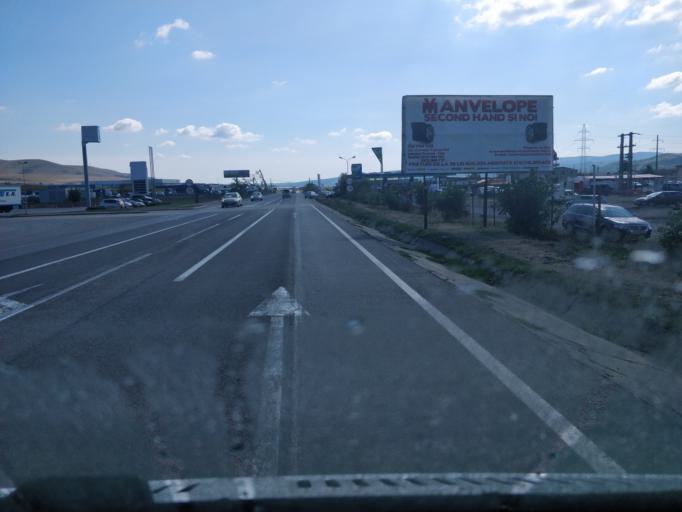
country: RO
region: Cluj
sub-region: Comuna Floresti
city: Luna de Sus
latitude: 46.7508
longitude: 23.4288
